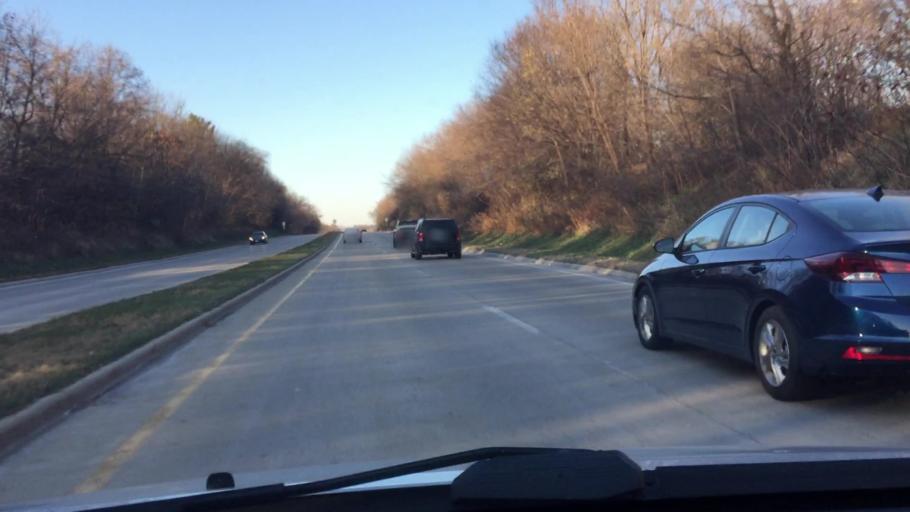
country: US
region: Wisconsin
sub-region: Waukesha County
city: Oconomowoc
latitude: 43.0993
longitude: -88.4803
